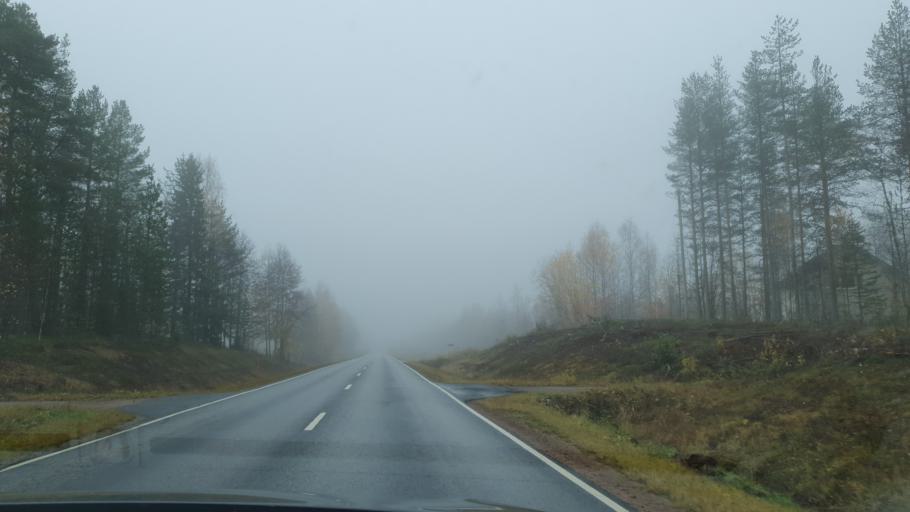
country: FI
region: Lapland
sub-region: Rovaniemi
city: Rovaniemi
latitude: 66.7948
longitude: 25.4152
